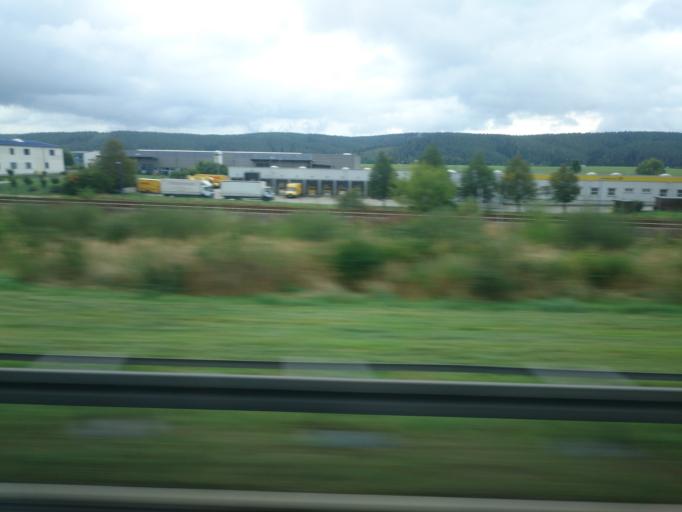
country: DE
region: Thuringia
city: Laasdorf
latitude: 50.8770
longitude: 11.6642
